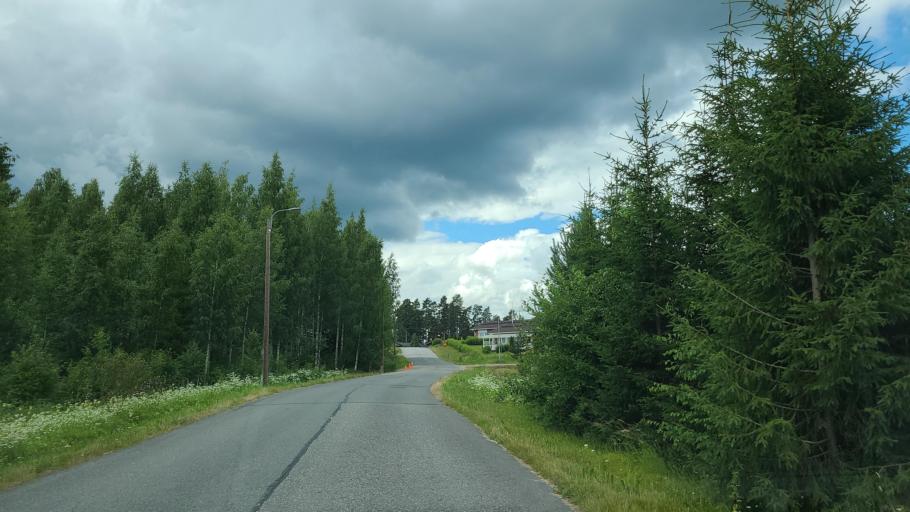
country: FI
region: Northern Savo
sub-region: Koillis-Savo
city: Kaavi
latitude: 62.9729
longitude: 28.4779
